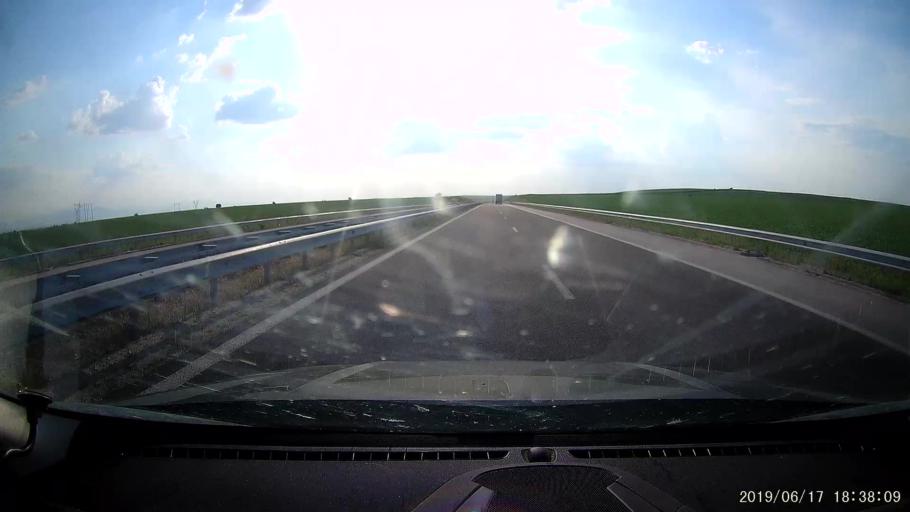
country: BG
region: Stara Zagora
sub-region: Obshtina Chirpan
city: Chirpan
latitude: 42.1353
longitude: 25.3442
